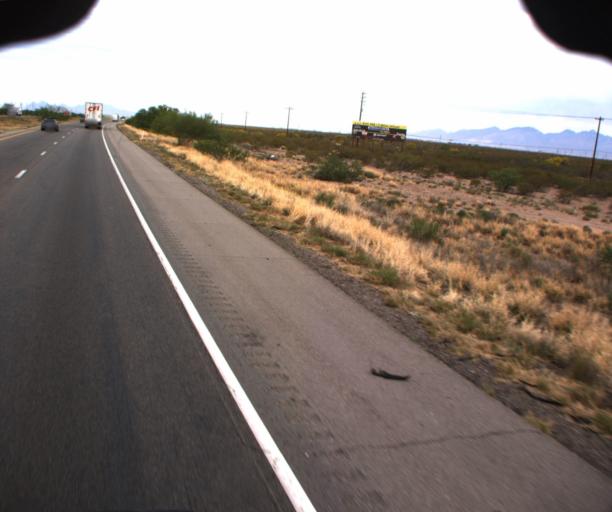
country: US
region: Arizona
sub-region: Pima County
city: Vail
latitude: 32.0473
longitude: -110.7505
